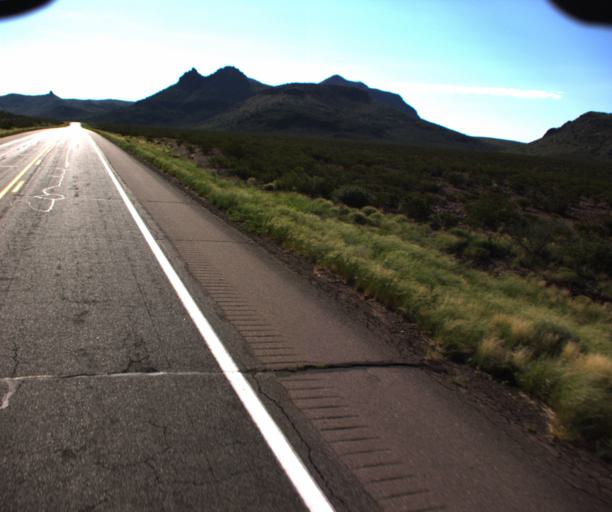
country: US
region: Arizona
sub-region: Greenlee County
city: Clifton
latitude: 32.8473
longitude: -109.3833
